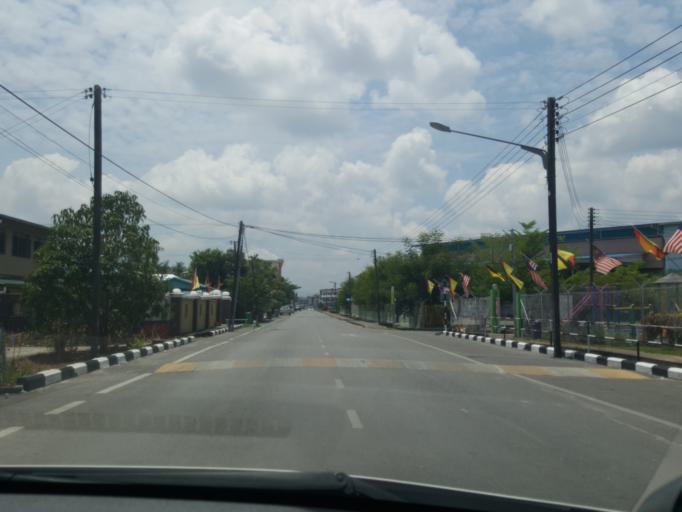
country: MY
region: Sarawak
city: Sarikei
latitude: 2.1282
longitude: 111.5185
